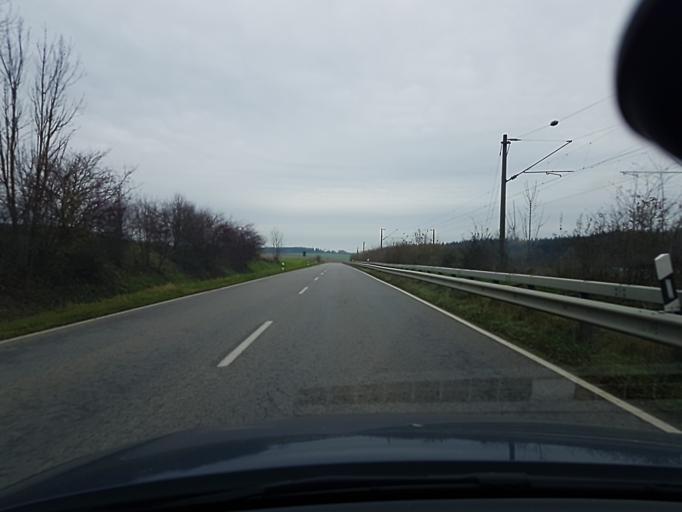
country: DE
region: Bavaria
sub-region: Upper Palatinate
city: Pfakofen
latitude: 48.8589
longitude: 12.1866
